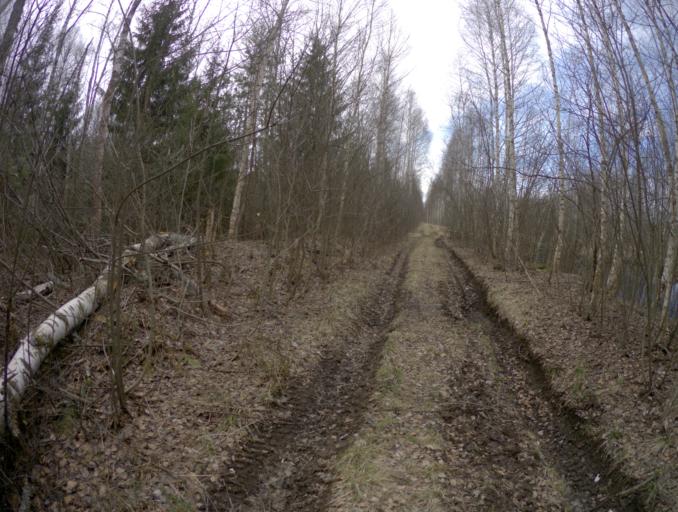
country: RU
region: Vladimir
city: Raduzhnyy
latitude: 55.8950
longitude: 40.2297
